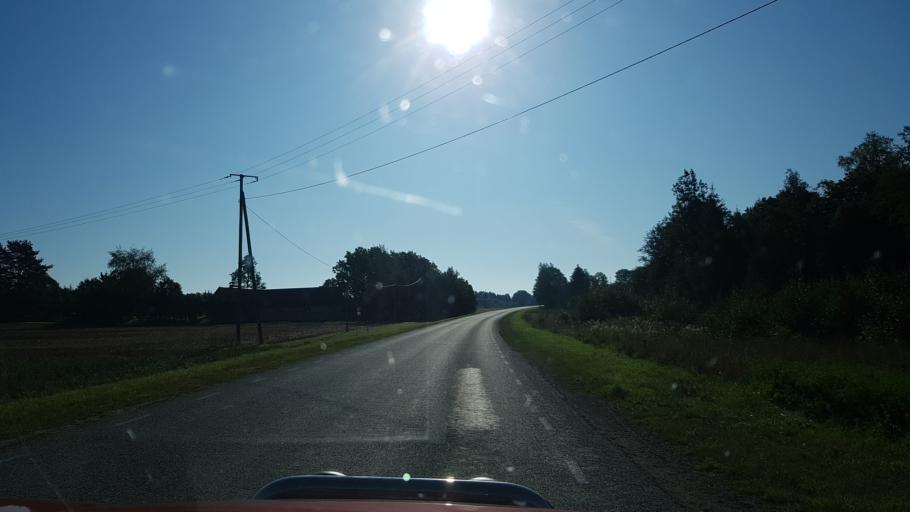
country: EE
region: Jogevamaa
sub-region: Tabivere vald
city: Tabivere
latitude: 58.6832
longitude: 26.6112
